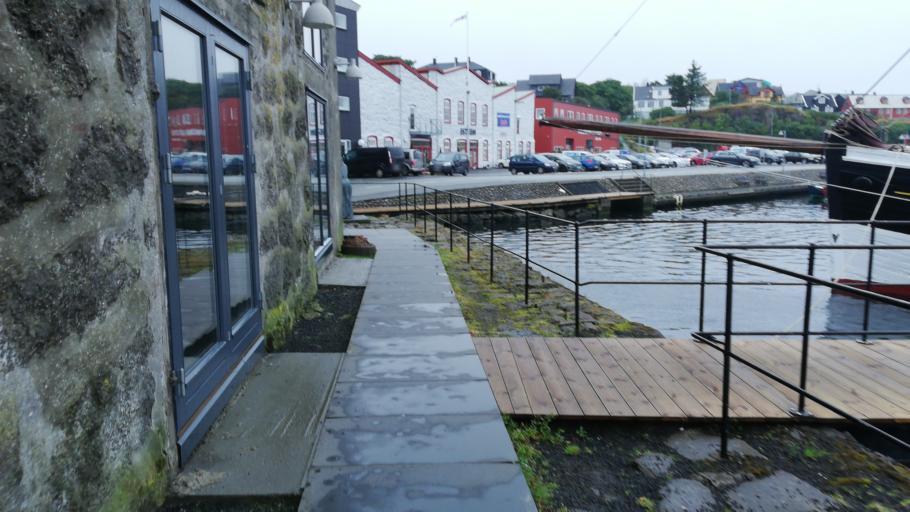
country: FO
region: Streymoy
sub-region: Torshavn
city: Torshavn
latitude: 62.0074
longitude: -6.7753
